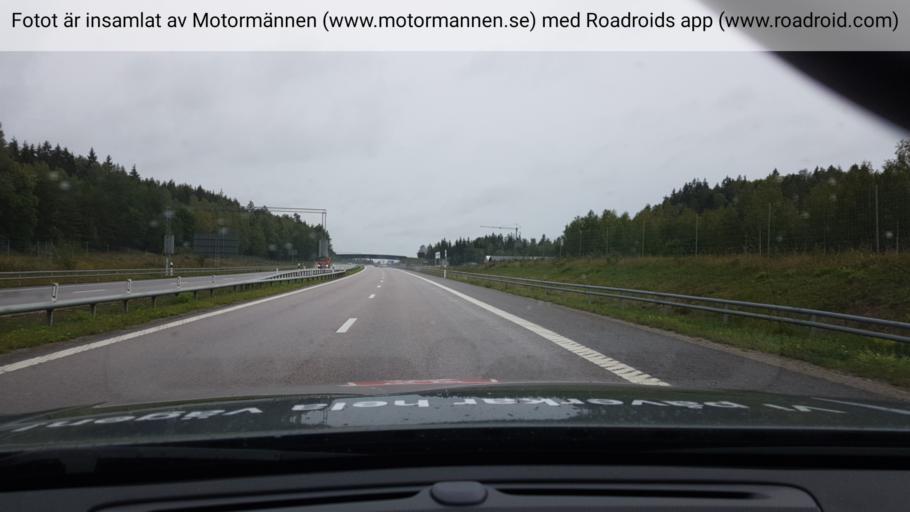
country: SE
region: Stockholm
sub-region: Nynashamns Kommun
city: Osmo
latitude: 58.9678
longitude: 17.9075
